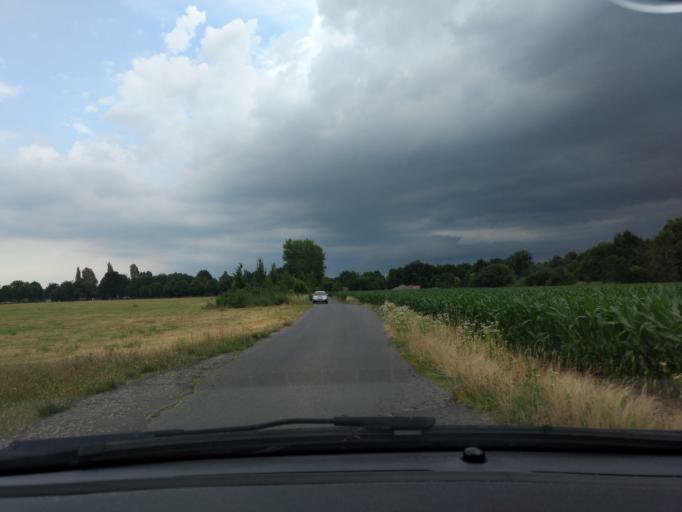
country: DE
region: Saxony
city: Radeburg
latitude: 51.2208
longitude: 13.7375
